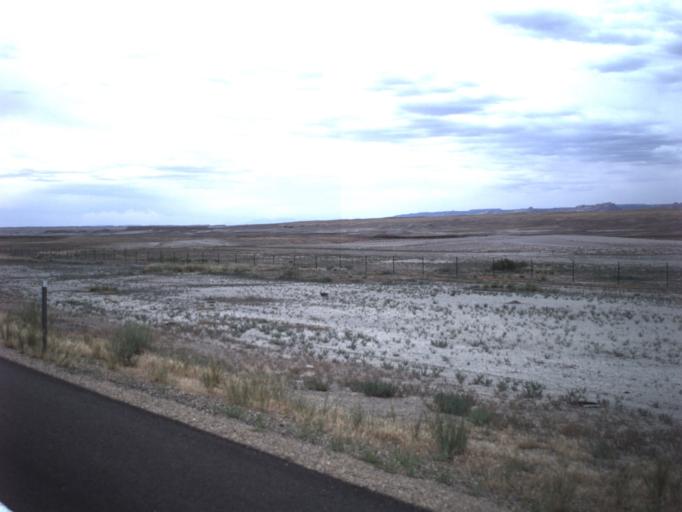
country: US
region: Utah
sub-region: Carbon County
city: East Carbon City
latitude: 39.0599
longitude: -110.3126
